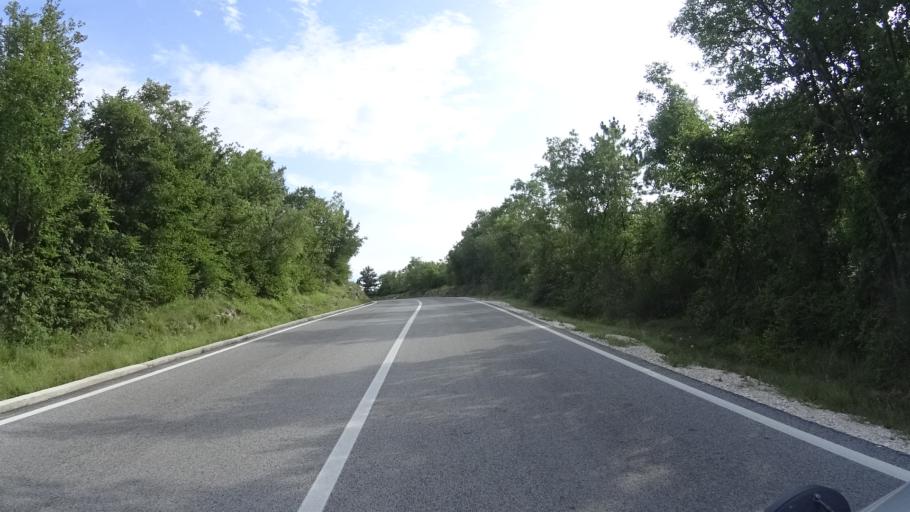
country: HR
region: Istarska
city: Rasa
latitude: 45.0521
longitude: 14.0835
